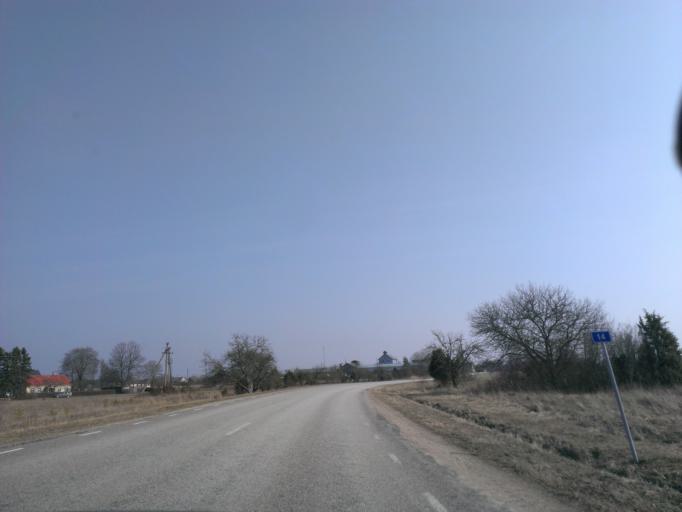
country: EE
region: Saare
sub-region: Kuressaare linn
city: Kuressaare
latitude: 58.3022
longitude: 22.6990
